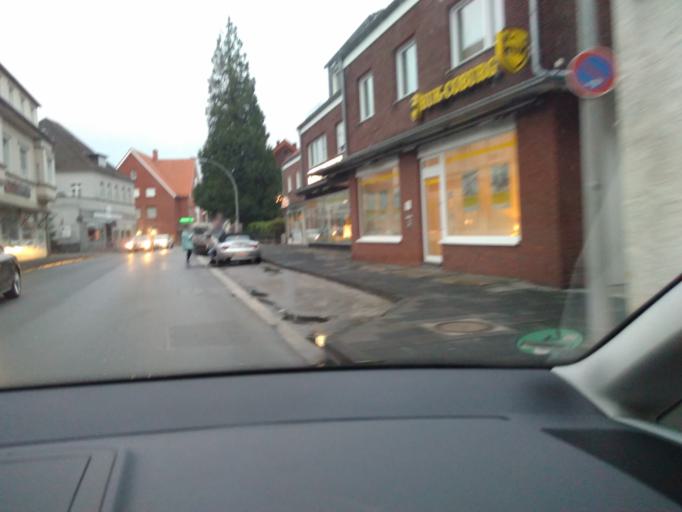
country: DE
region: North Rhine-Westphalia
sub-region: Regierungsbezirk Detmold
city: Rheda-Wiedenbruck
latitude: 51.8332
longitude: 8.3118
